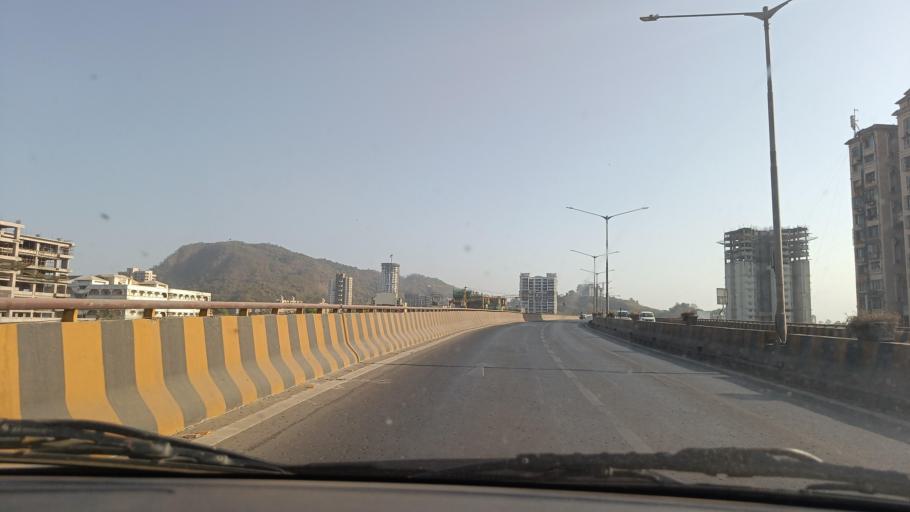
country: IN
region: Maharashtra
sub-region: Mumbai Suburban
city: Mumbai
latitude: 19.0506
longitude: 72.9106
